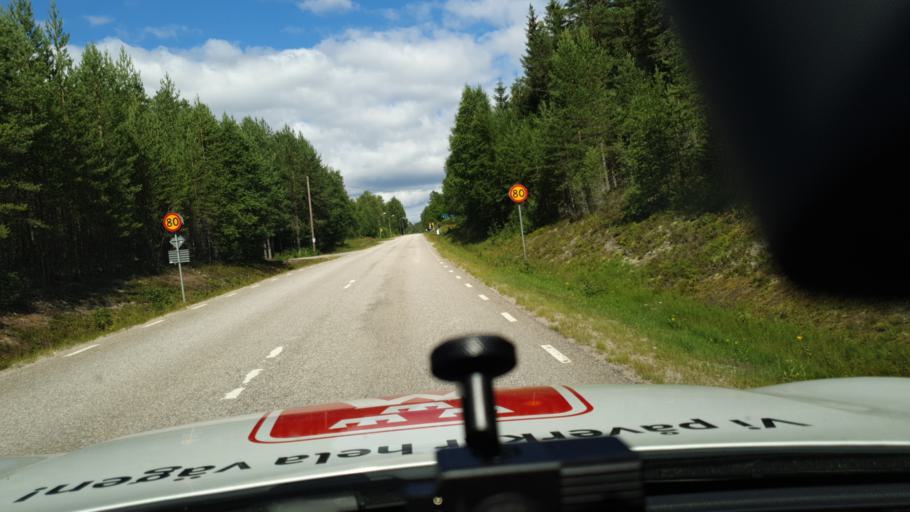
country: NO
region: Hedmark
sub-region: Trysil
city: Innbygda
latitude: 60.9595
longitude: 12.4717
